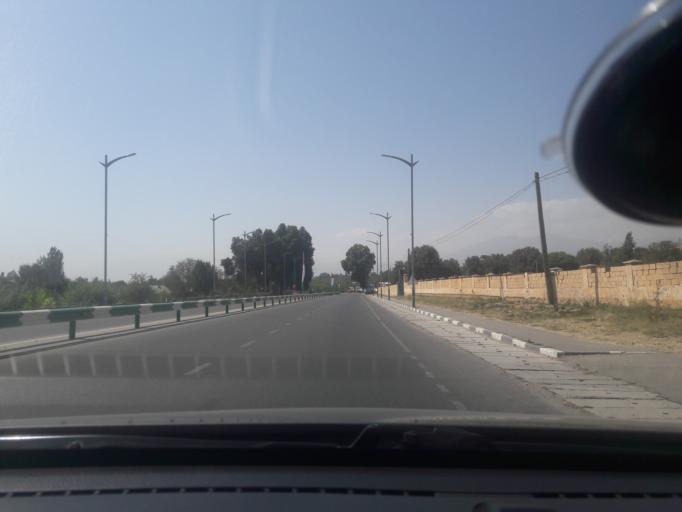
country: TJ
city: Shahrinav
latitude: 38.5631
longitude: 68.4153
